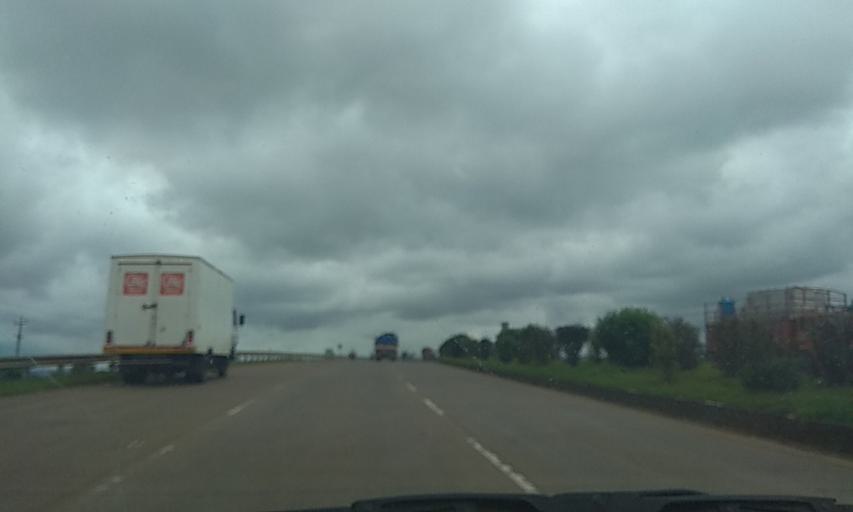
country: IN
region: Karnataka
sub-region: Belgaum
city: Belgaum
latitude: 15.8082
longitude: 74.5699
